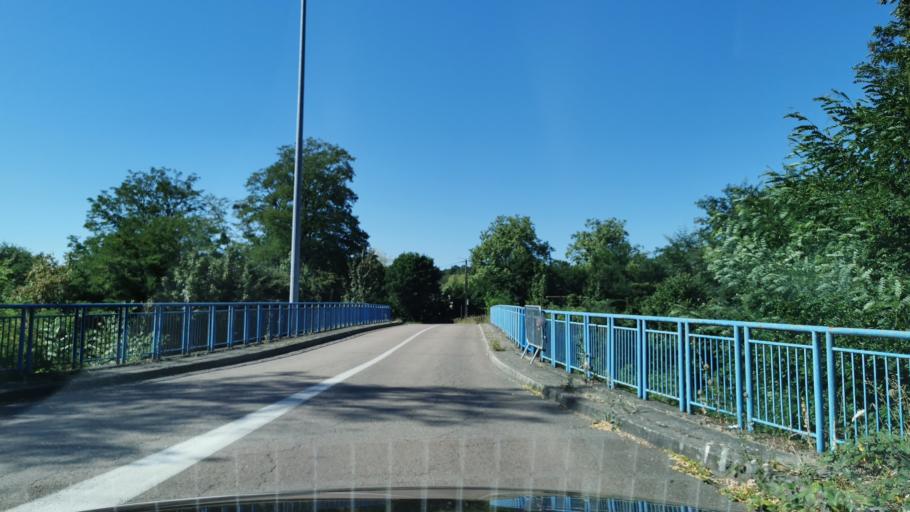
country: FR
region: Bourgogne
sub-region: Departement de Saone-et-Loire
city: Montchanin
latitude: 46.7614
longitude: 4.4765
